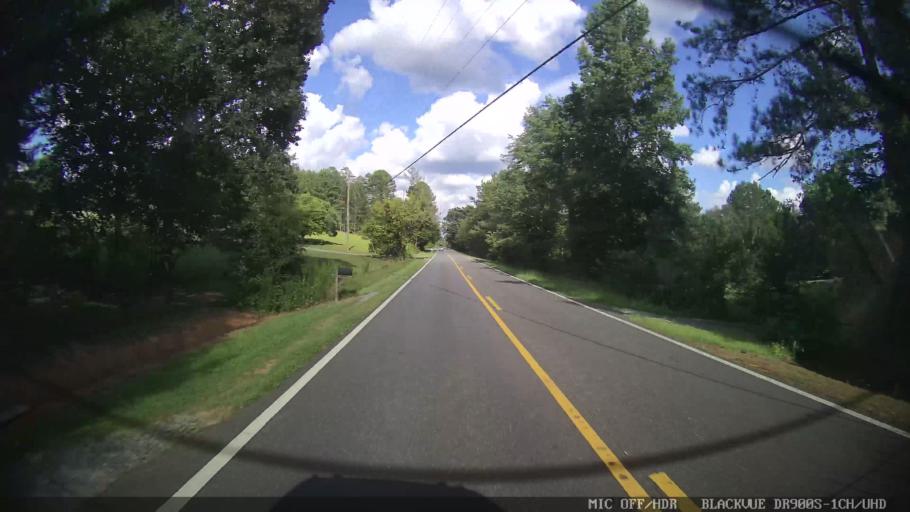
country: US
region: Georgia
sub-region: Bartow County
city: Euharlee
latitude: 34.1770
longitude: -85.0013
